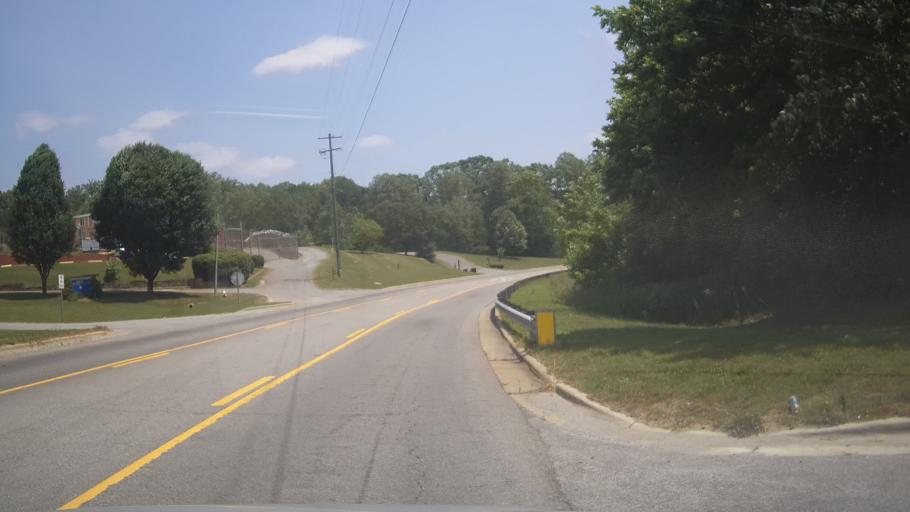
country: US
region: North Carolina
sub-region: McDowell County
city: Marion
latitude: 35.6522
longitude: -81.9555
